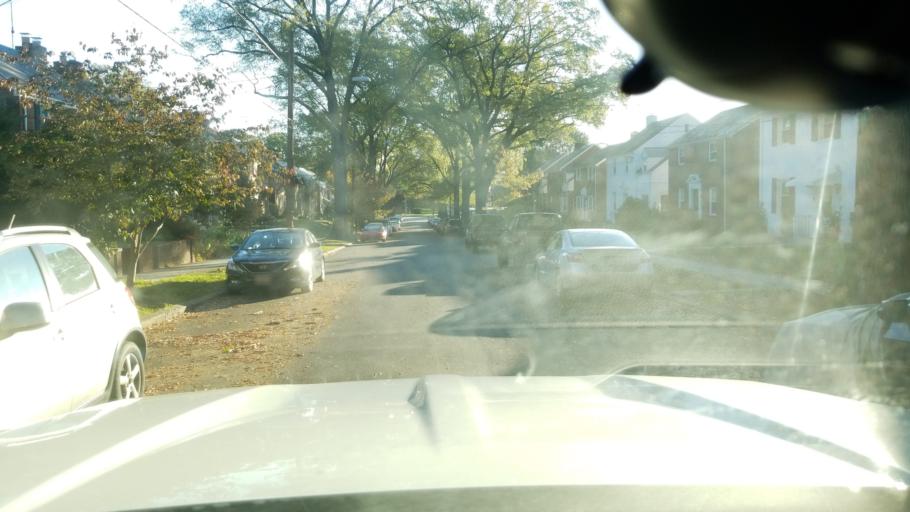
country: US
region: Maryland
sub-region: Prince George's County
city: Mount Rainier
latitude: 38.9434
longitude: -76.9824
